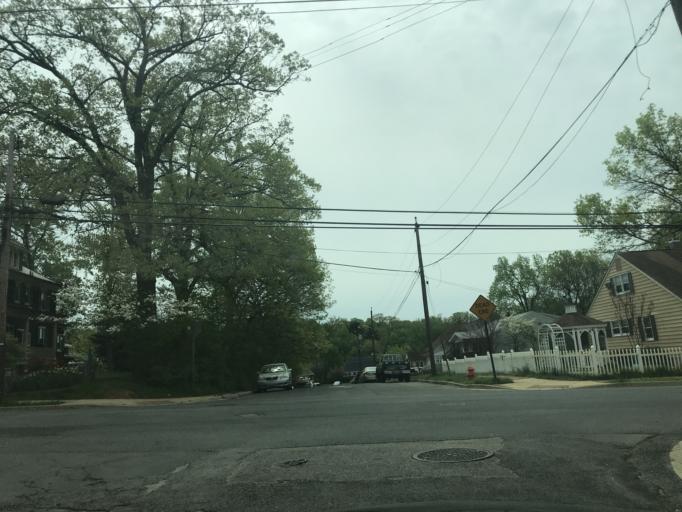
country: US
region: Maryland
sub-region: Baltimore County
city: Catonsville
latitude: 39.2646
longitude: -76.7337
